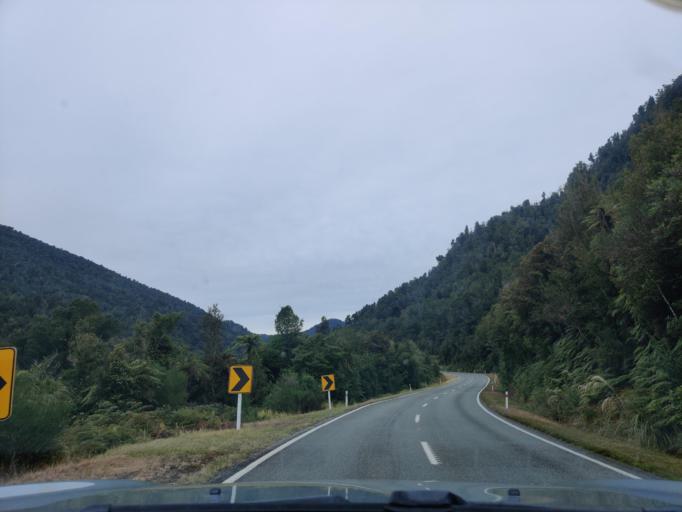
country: NZ
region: West Coast
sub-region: Buller District
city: Westport
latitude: -41.8522
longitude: 171.7462
